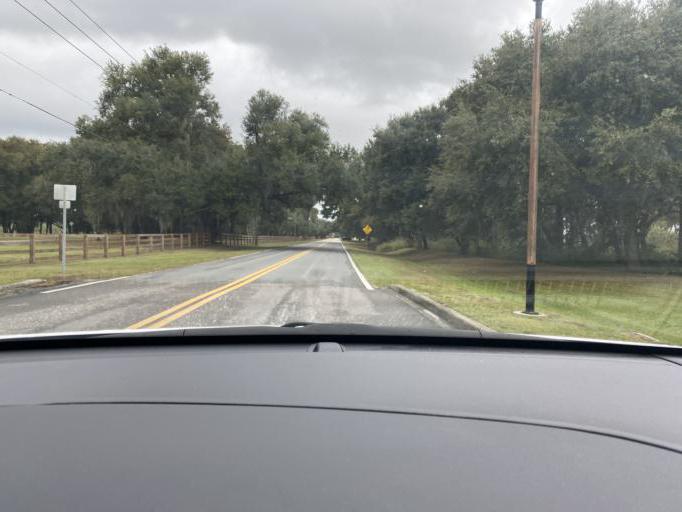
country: US
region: Florida
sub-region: Lake County
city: Clermont
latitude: 28.5713
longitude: -81.7804
